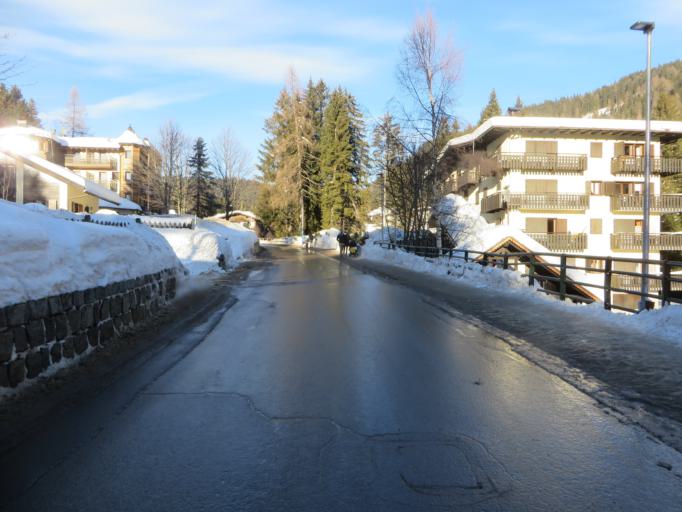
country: IT
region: Trentino-Alto Adige
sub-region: Provincia di Trento
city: Carisolo
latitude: 46.2228
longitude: 10.8256
